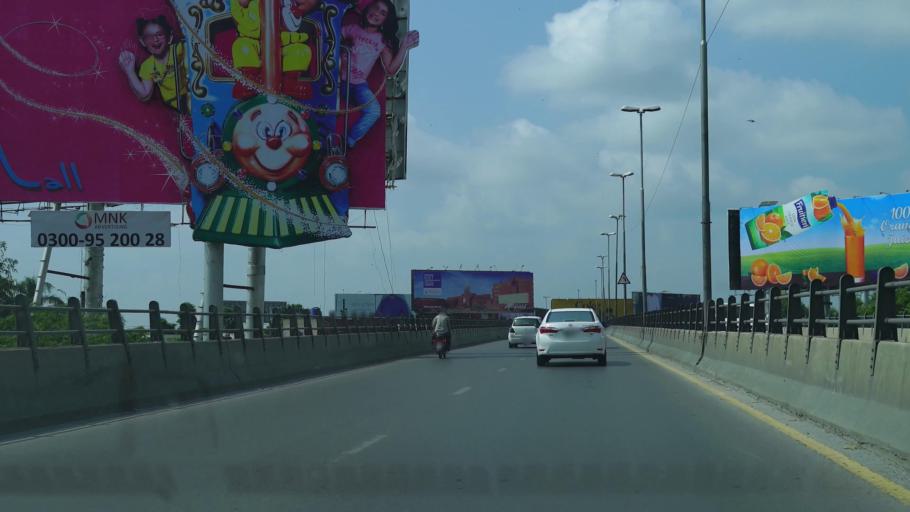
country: PK
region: Punjab
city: Lahore
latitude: 31.5286
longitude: 74.3603
